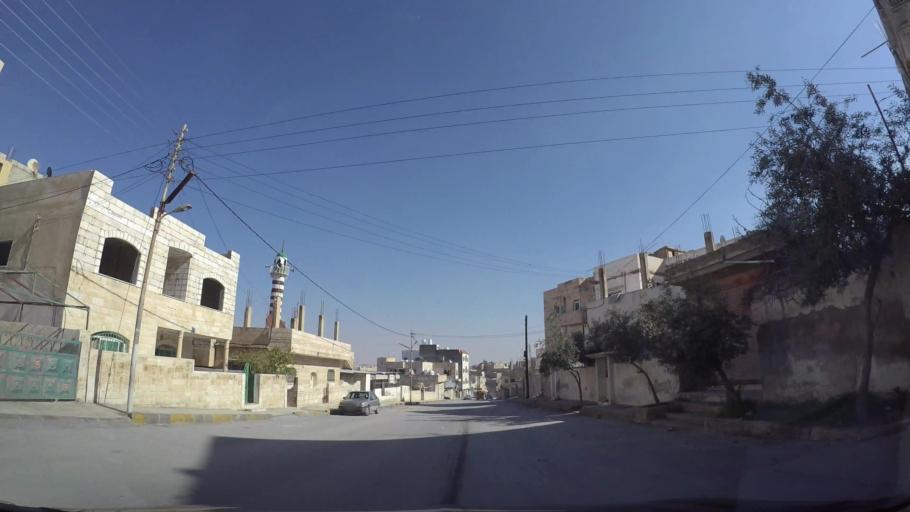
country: JO
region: Zarqa
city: Russeifa
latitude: 32.0340
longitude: 36.0369
